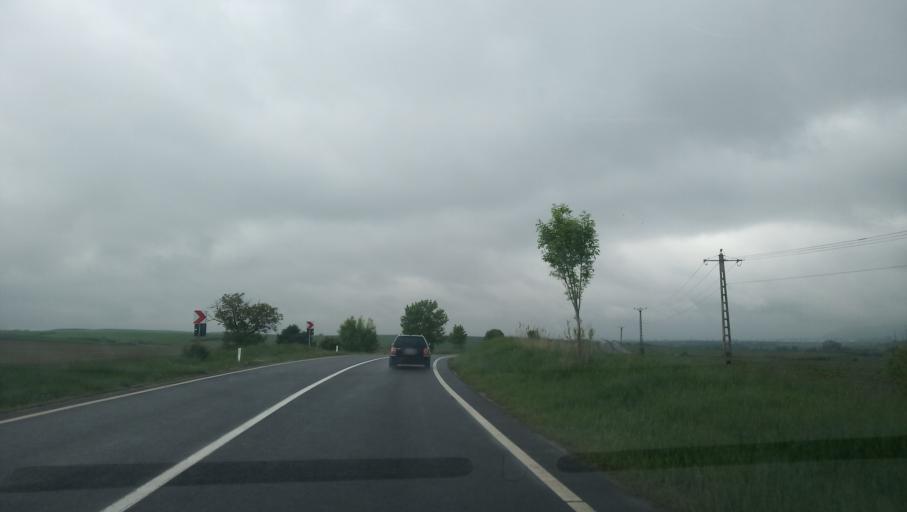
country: RO
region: Alba
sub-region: Municipiul Sebes
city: Sebes
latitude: 45.9278
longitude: 23.6113
